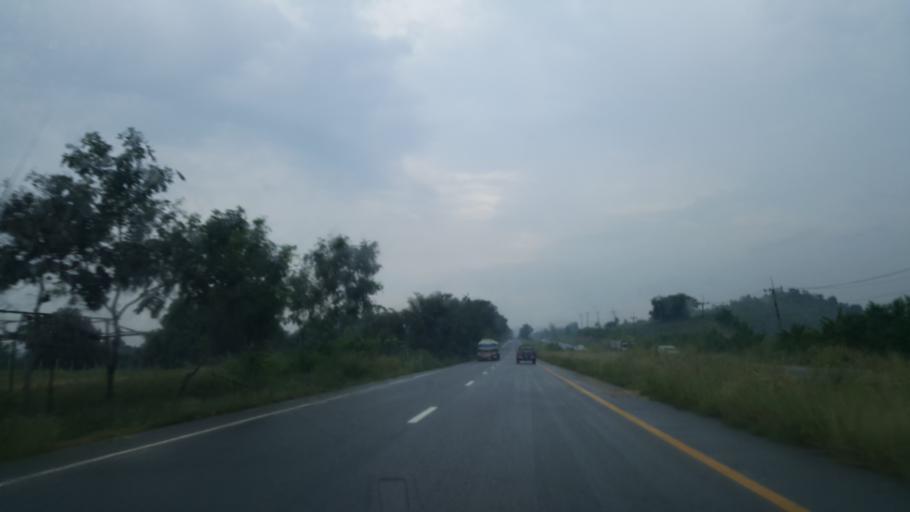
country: TH
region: Rayong
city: Ban Chang
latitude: 12.8559
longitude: 101.0207
